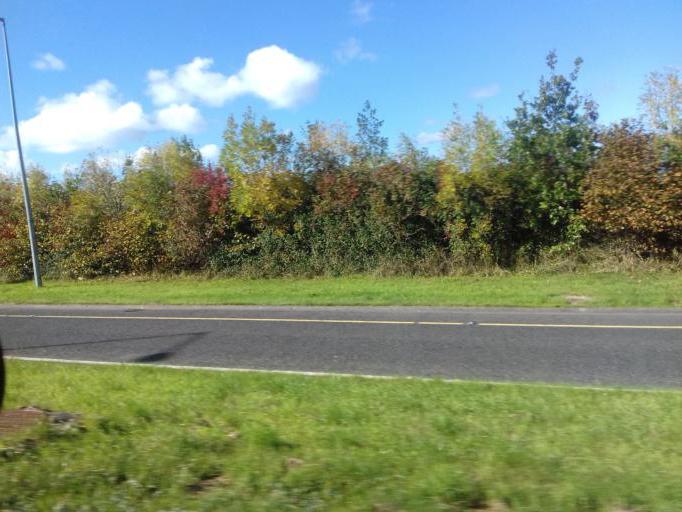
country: IE
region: Leinster
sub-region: An Mhi
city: Ashbourne
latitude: 53.4905
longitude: -6.3873
